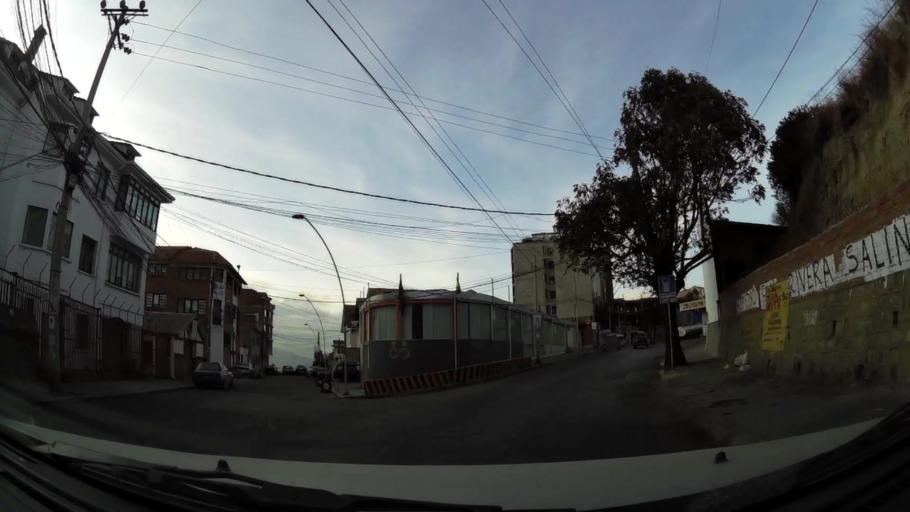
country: BO
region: La Paz
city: La Paz
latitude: -16.5133
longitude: -68.1248
